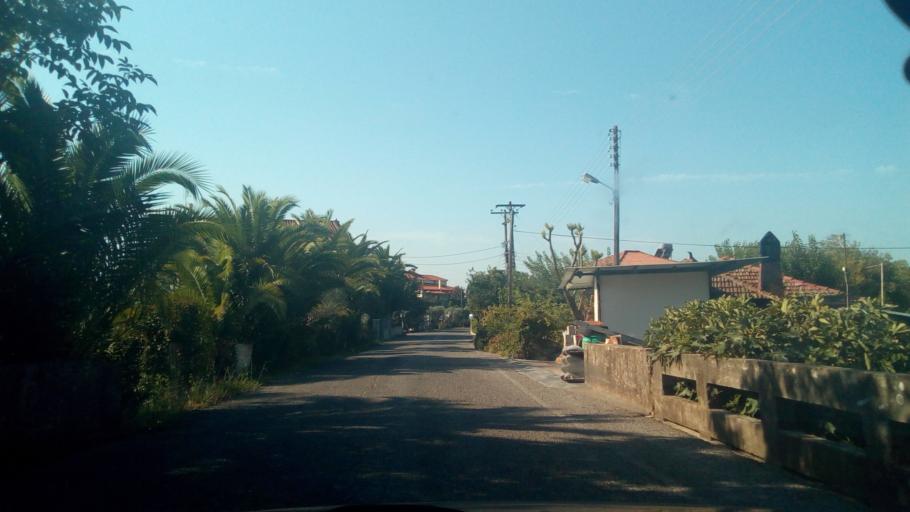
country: GR
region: West Greece
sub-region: Nomos Aitolias kai Akarnanias
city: Nafpaktos
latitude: 38.4181
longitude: 21.8875
